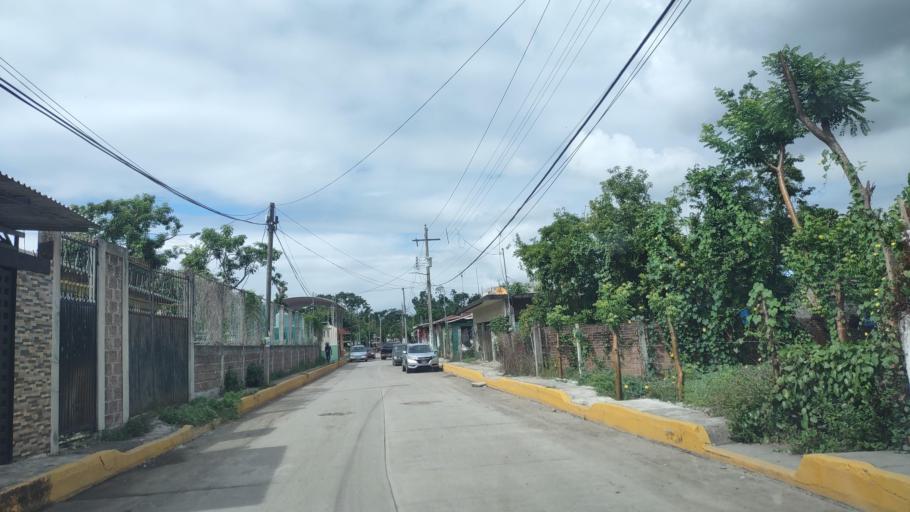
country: MX
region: Veracruz
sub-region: Papantla
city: Residencial Tajin
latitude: 20.5958
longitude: -97.4211
